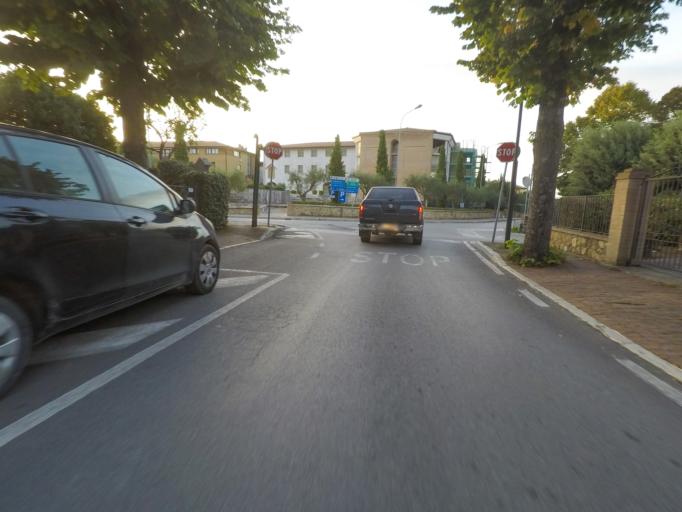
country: IT
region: Tuscany
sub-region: Provincia di Siena
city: Pienza
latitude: 43.0781
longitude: 11.6782
